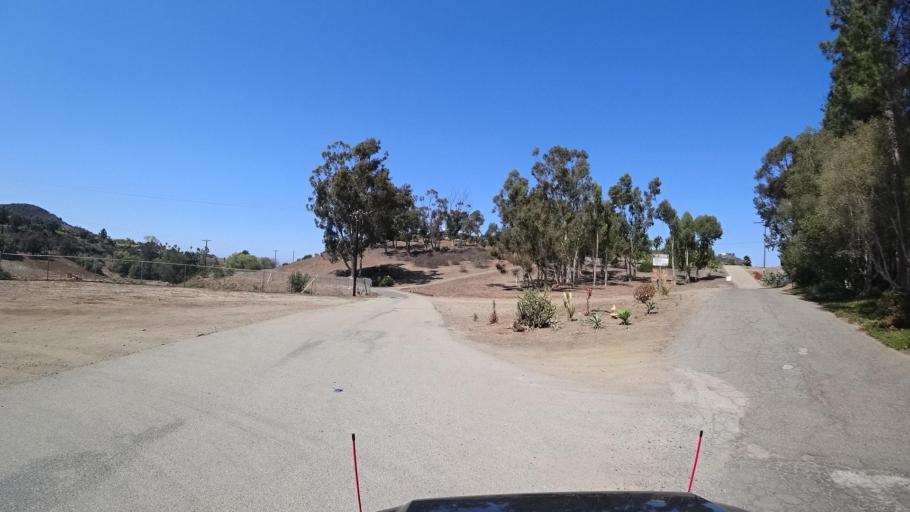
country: US
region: California
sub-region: San Diego County
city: San Marcos
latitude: 33.1853
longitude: -117.1776
